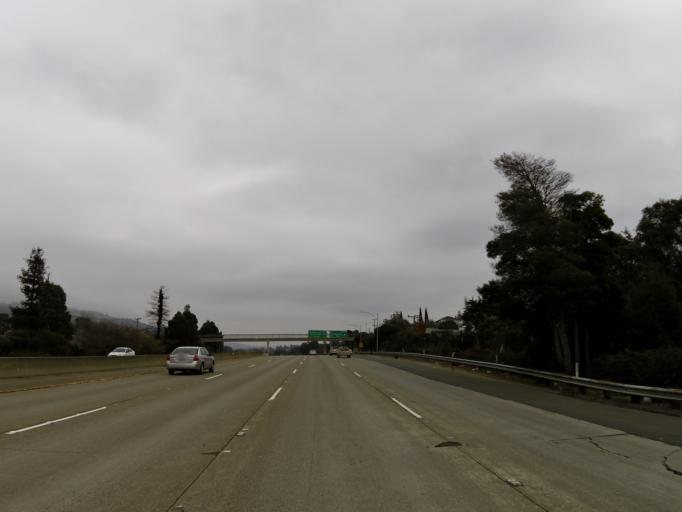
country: US
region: California
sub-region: Alameda County
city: Alameda
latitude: 37.7865
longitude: -122.1955
